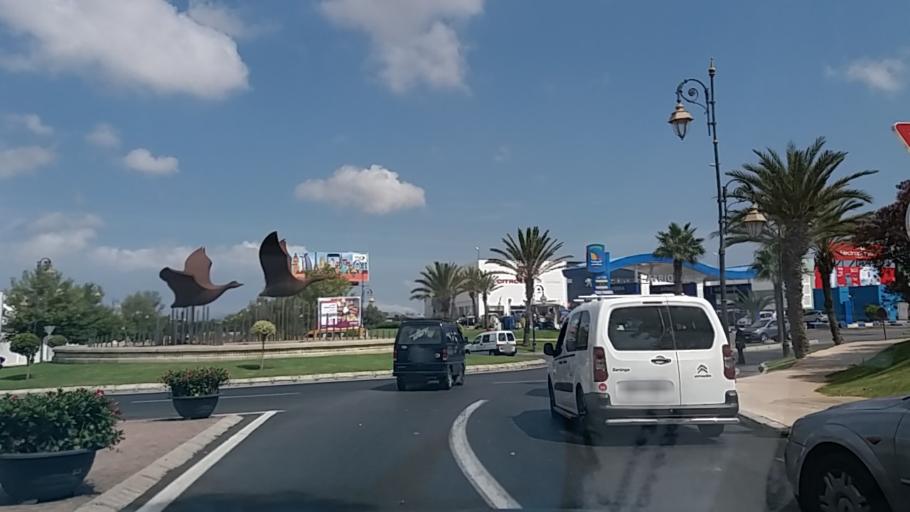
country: MA
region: Tanger-Tetouan
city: Tetouan
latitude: 35.6037
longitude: -5.3357
